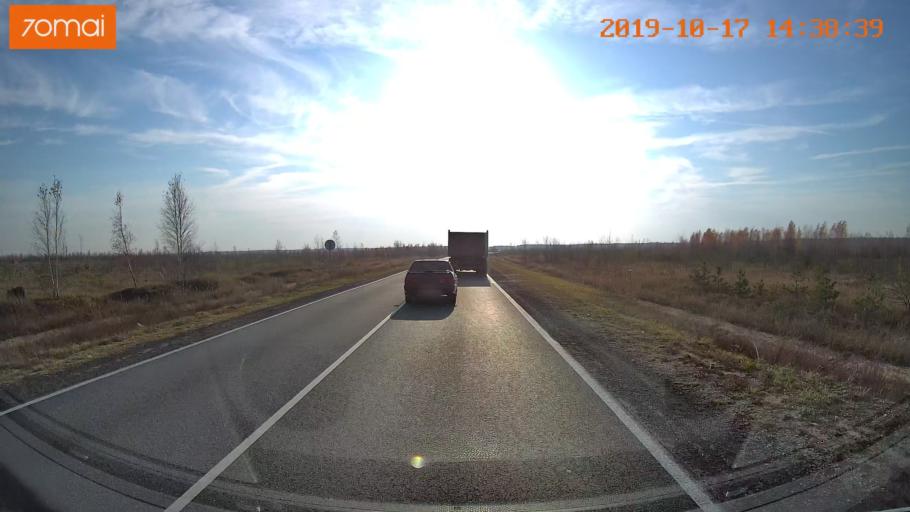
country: RU
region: Rjazan
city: Solotcha
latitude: 54.8683
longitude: 39.9832
